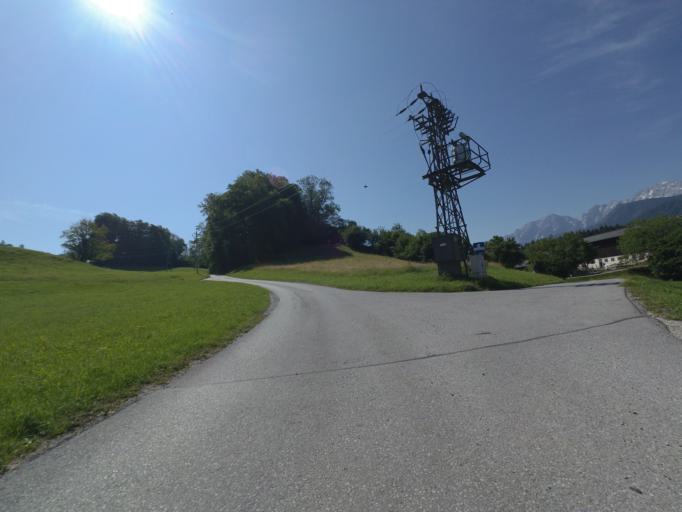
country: AT
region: Salzburg
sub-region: Politischer Bezirk Hallein
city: Adnet
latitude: 47.6866
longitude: 13.1246
